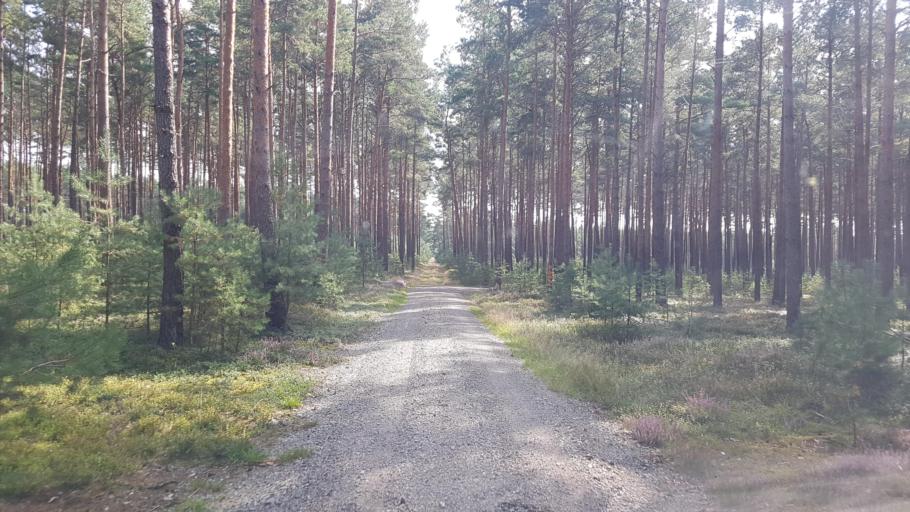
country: DE
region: Brandenburg
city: Hohenbucko
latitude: 51.7628
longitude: 13.5452
